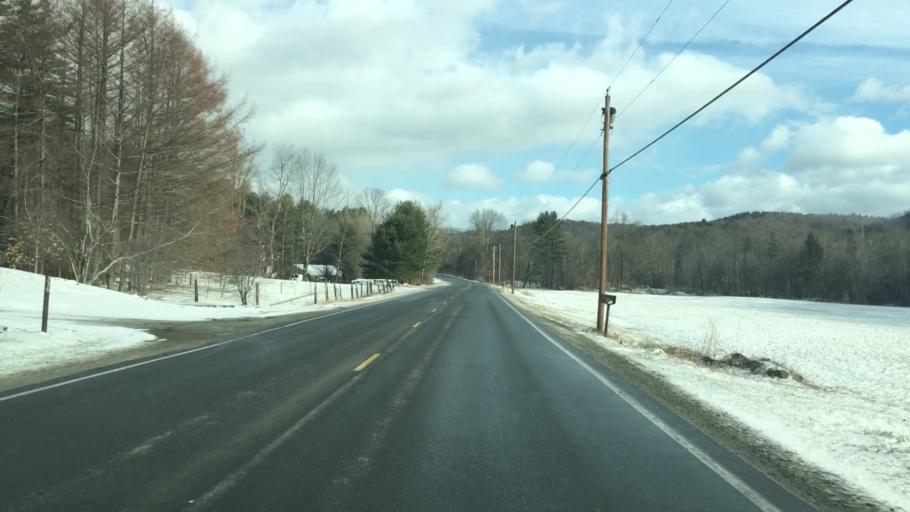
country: US
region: Massachusetts
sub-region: Franklin County
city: Colrain
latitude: 42.7148
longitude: -72.7051
